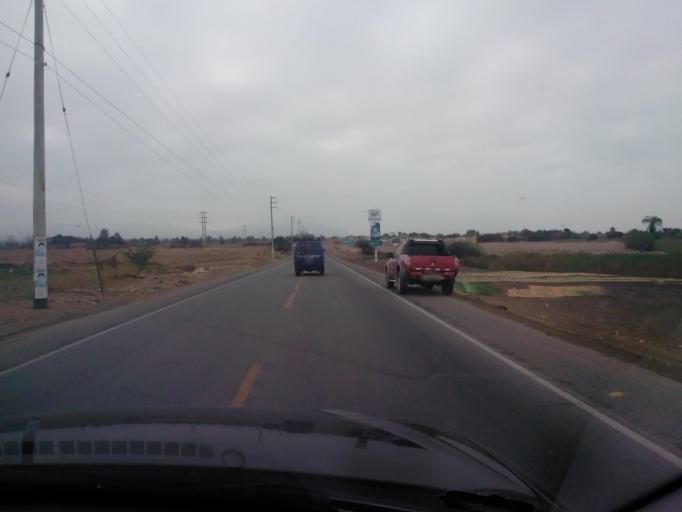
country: PE
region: Ica
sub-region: Provincia de Pisco
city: Independencia
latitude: -13.6849
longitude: -76.0487
